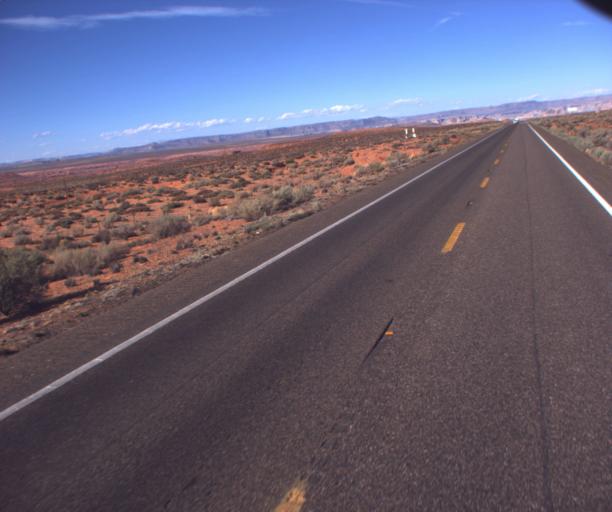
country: US
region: Arizona
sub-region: Coconino County
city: Page
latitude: 36.8633
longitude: -111.5046
